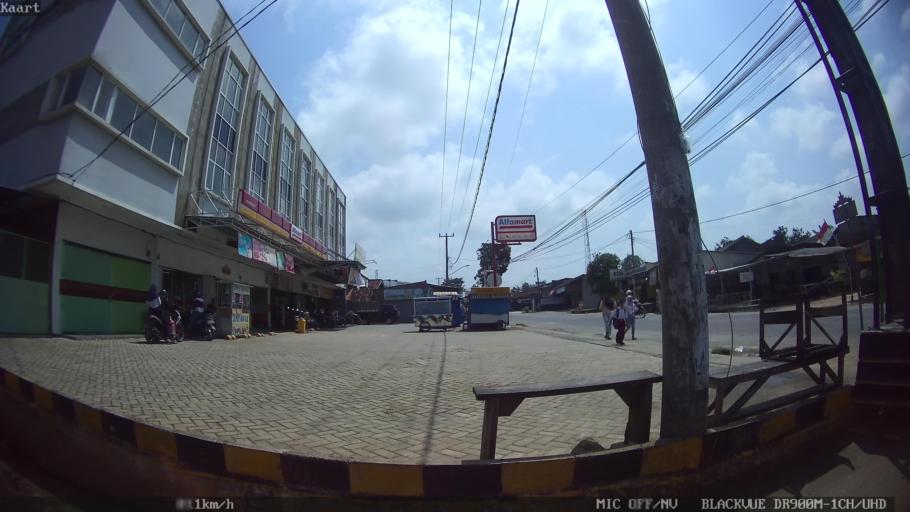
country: ID
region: Lampung
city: Kedaton
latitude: -5.3568
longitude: 105.2871
